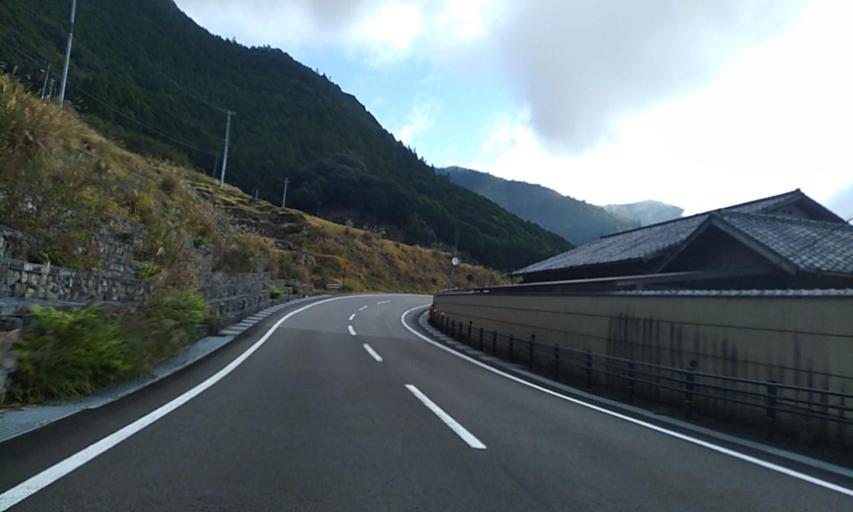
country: JP
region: Wakayama
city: Shingu
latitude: 33.8777
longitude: 135.8626
